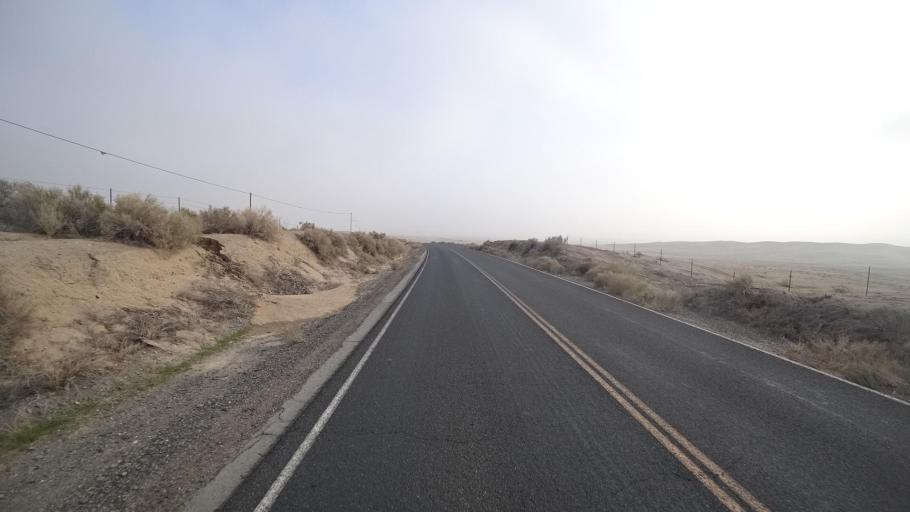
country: US
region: California
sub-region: Kern County
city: Ford City
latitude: 35.2477
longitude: -119.4612
